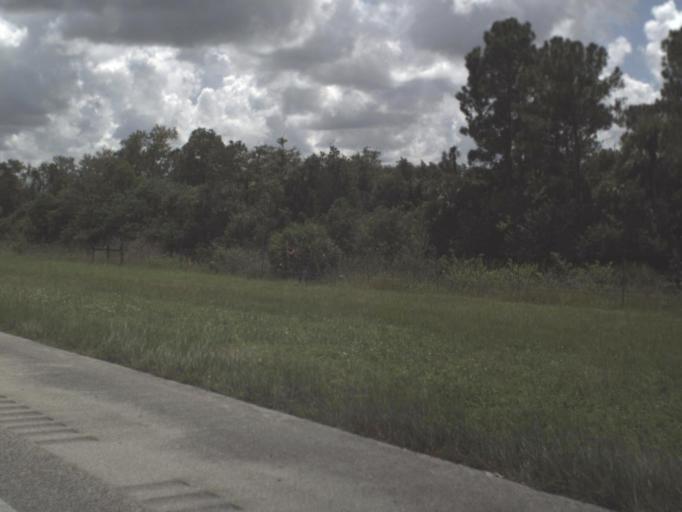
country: US
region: Florida
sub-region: Collier County
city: Orangetree
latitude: 26.1529
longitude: -81.5296
